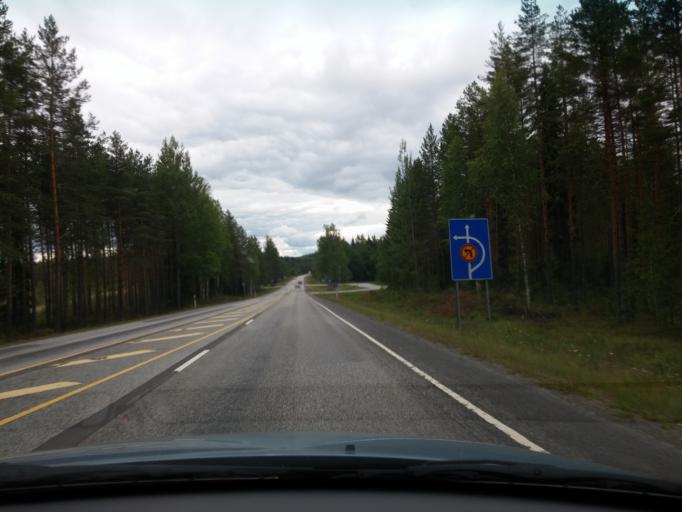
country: FI
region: Central Finland
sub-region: AEaenekoski
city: AEaenekoski
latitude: 62.7012
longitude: 25.7644
